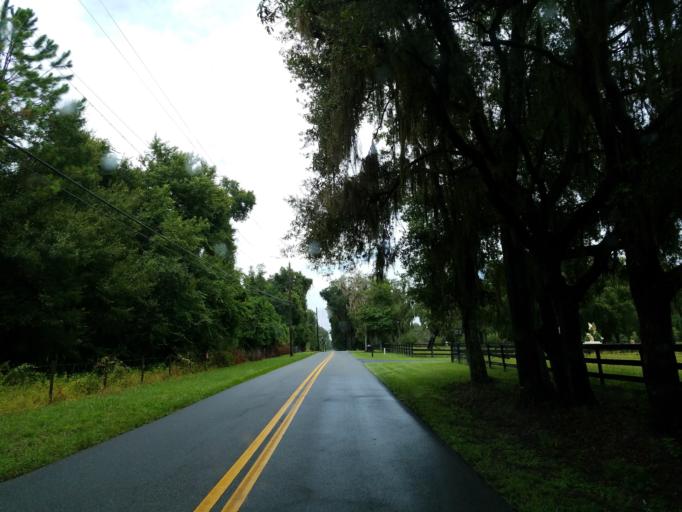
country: US
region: Florida
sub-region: Citrus County
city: Inverness Highlands South
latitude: 28.7948
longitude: -82.2951
